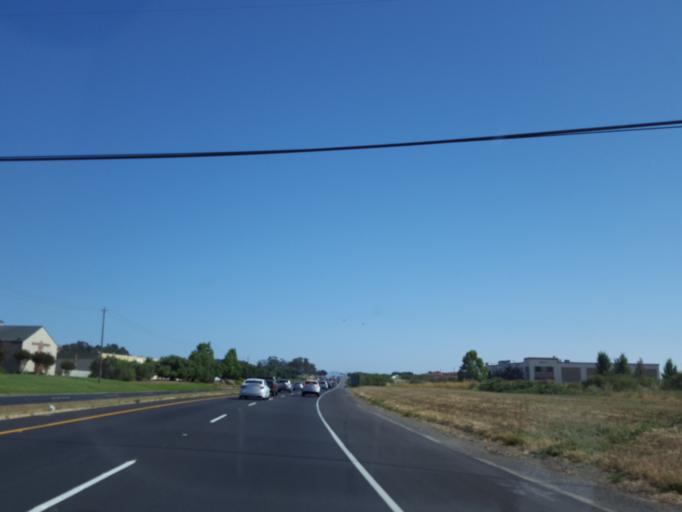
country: US
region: California
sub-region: Napa County
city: American Canyon
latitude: 38.2315
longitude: -122.2590
